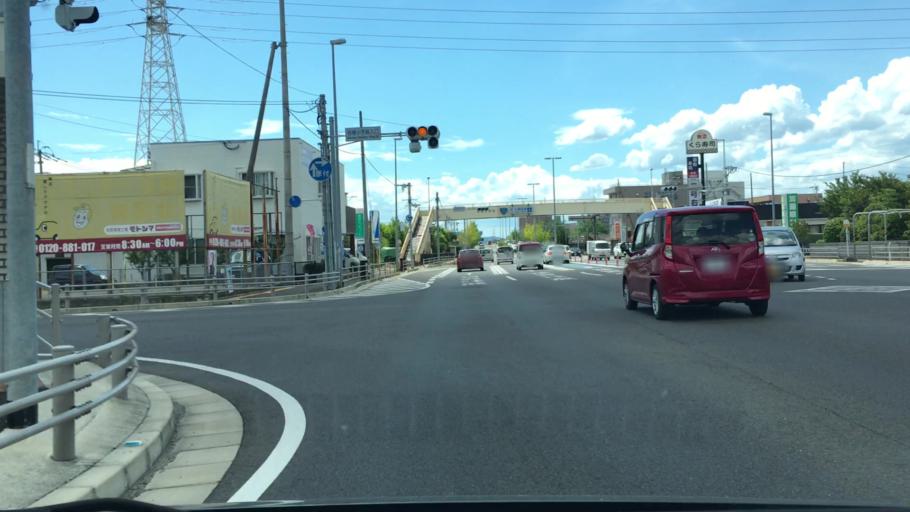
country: JP
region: Saga Prefecture
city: Saga-shi
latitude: 33.2732
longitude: 130.2865
